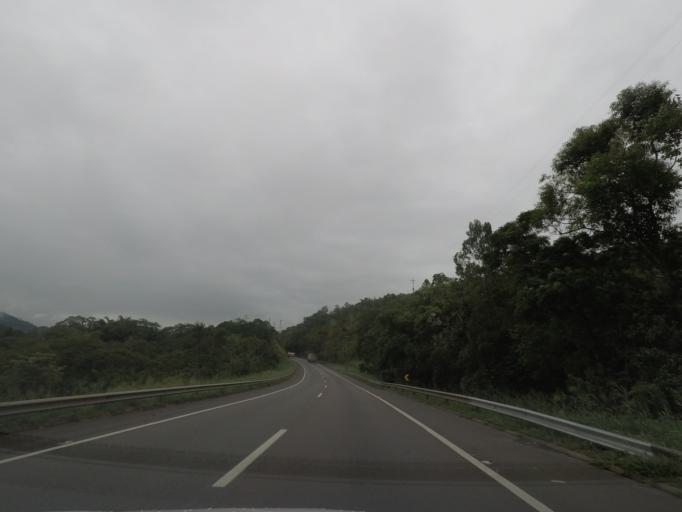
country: BR
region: Sao Paulo
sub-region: Cajati
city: Cajati
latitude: -24.7867
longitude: -48.2033
